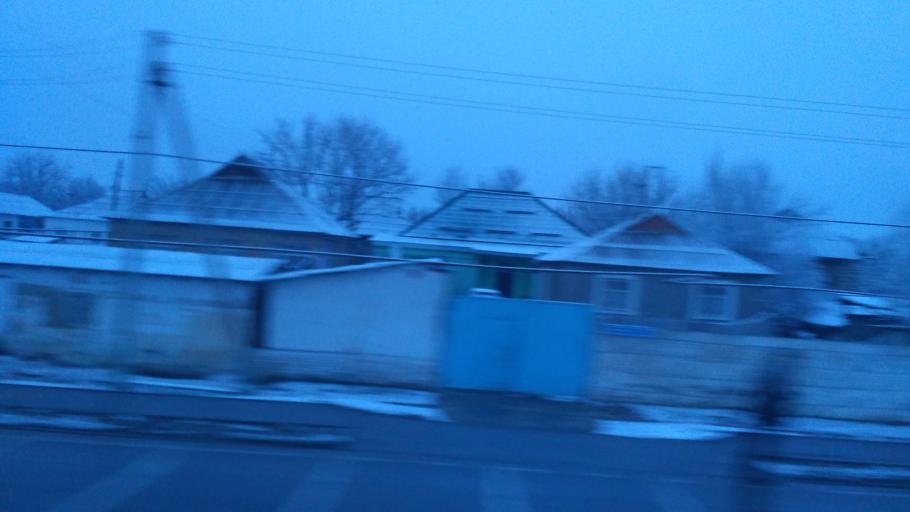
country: KZ
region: Ongtustik Qazaqstan
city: Shymkent
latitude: 42.3769
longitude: 69.4985
